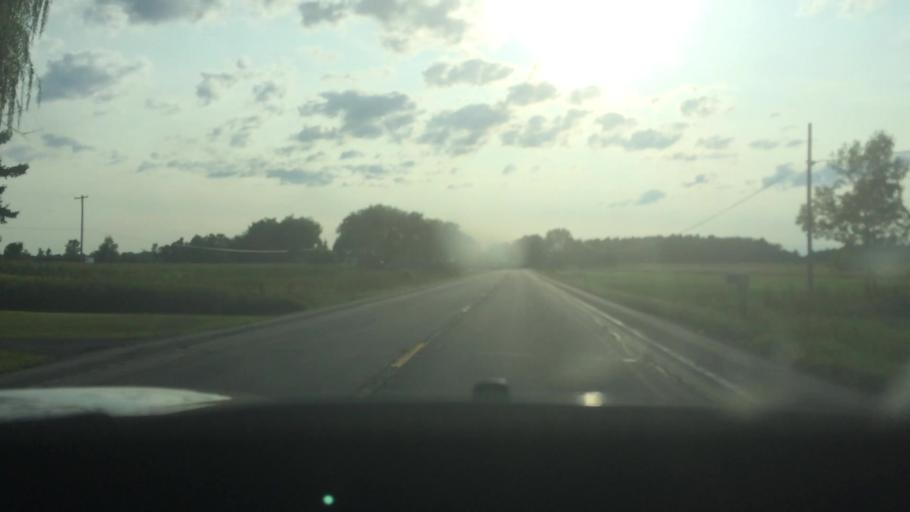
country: US
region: New York
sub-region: St. Lawrence County
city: Ogdensburg
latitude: 44.6745
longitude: -75.4090
